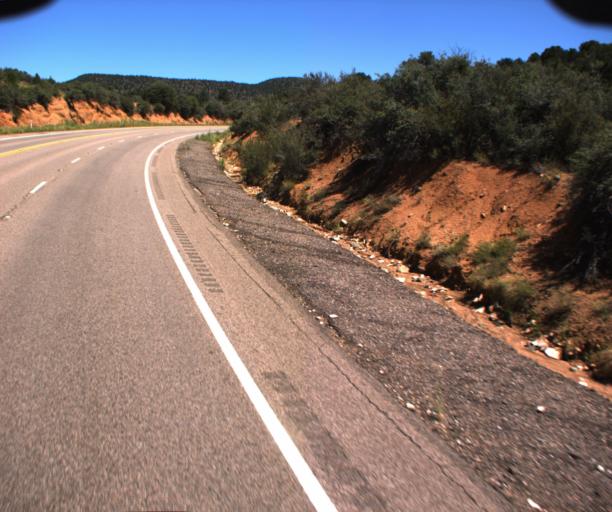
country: US
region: Arizona
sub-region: Gila County
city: Globe
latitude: 33.6360
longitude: -110.5844
